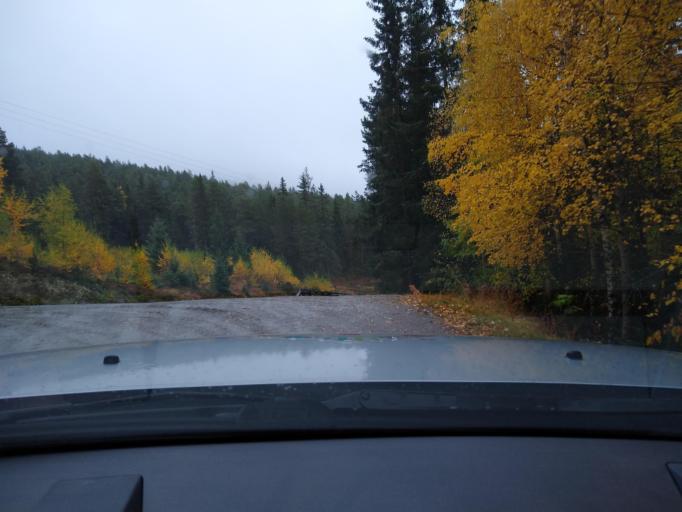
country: NO
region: Oppland
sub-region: Ringebu
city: Ringebu
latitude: 61.5503
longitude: 10.1572
